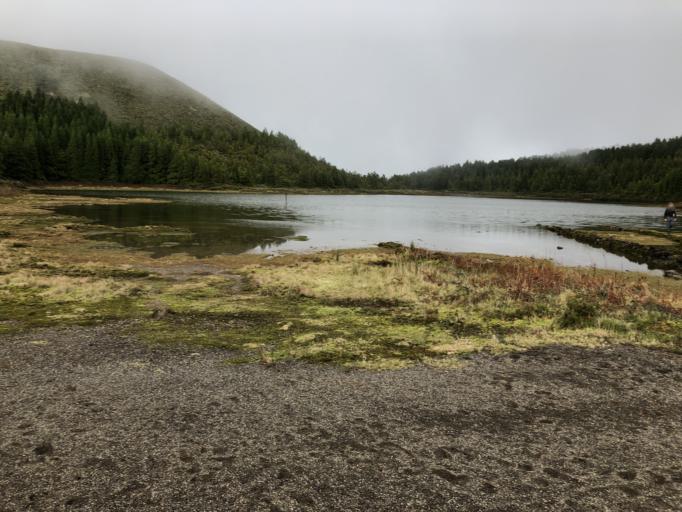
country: PT
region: Azores
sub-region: Ponta Delgada
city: Arrifes
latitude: 37.8237
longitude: -25.7519
